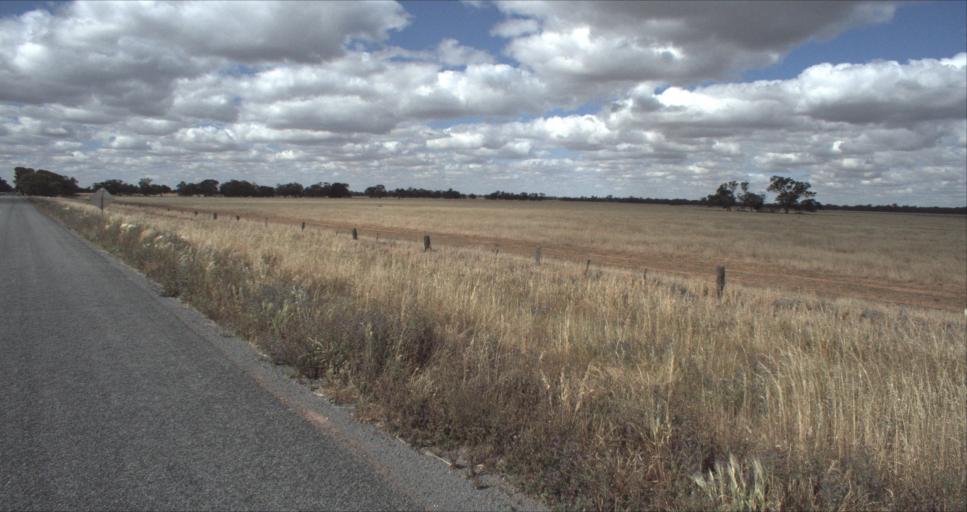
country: AU
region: New South Wales
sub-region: Leeton
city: Leeton
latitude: -34.6960
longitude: 146.3428
